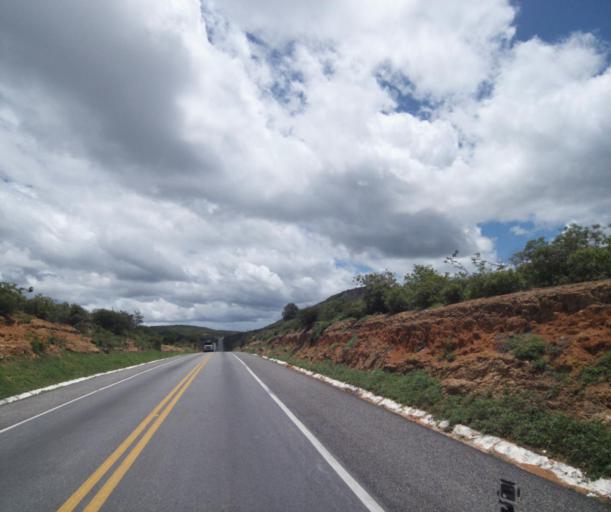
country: BR
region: Bahia
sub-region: Pocoes
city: Pocoes
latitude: -14.3788
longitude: -40.3483
